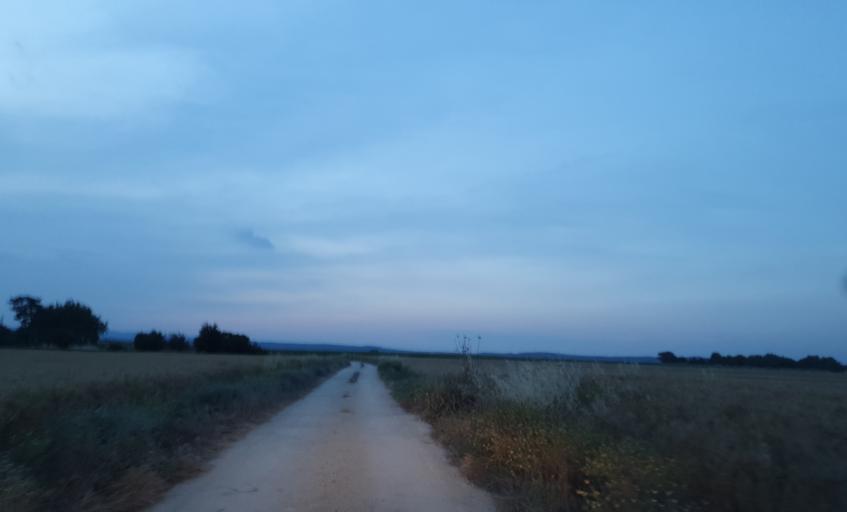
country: TR
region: Kirklareli
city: Vize
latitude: 41.5155
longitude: 27.7449
